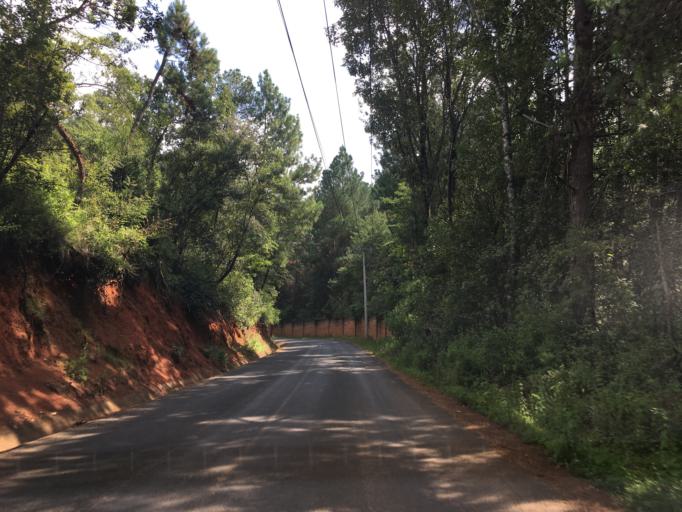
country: MX
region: Michoacan
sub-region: Morelia
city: Montana Monarca (Punta Altozano)
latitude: 19.5728
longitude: -101.1891
